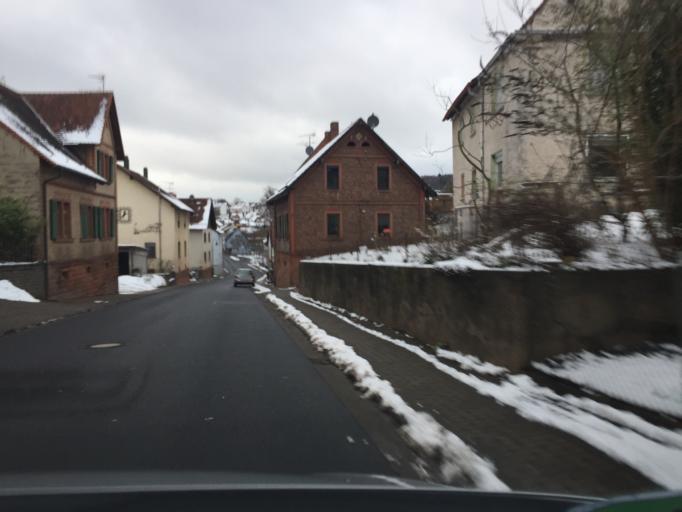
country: DE
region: Bavaria
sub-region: Regierungsbezirk Unterfranken
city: Geiselbach
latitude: 50.1202
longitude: 9.2000
